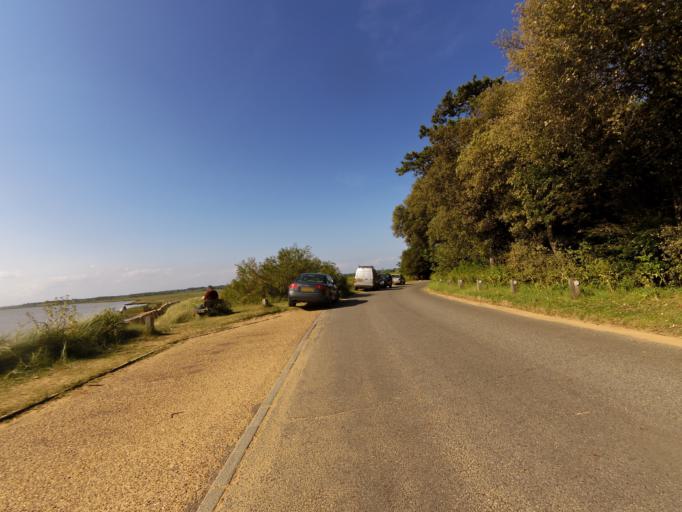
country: GB
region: England
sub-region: Suffolk
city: Felixstowe
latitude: 51.9926
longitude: 1.3948
